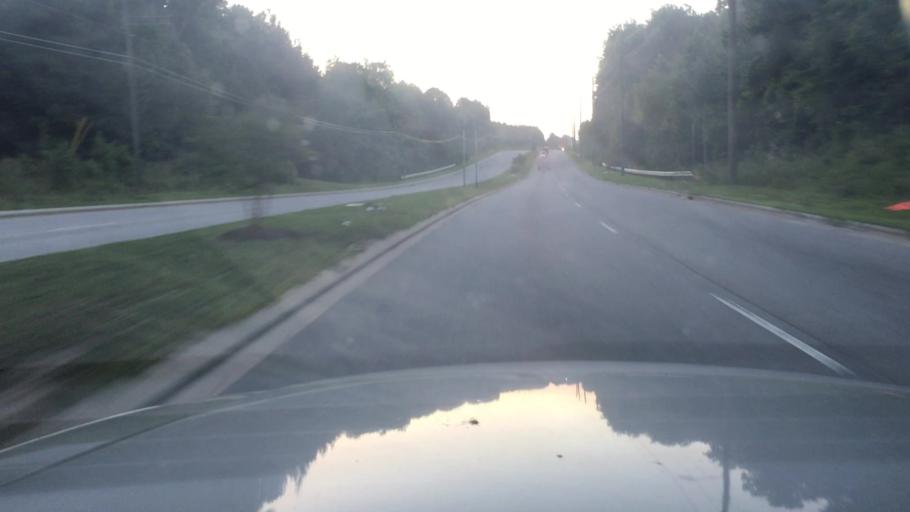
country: US
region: North Carolina
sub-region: Hoke County
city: Rockfish
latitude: 35.0650
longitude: -79.0340
